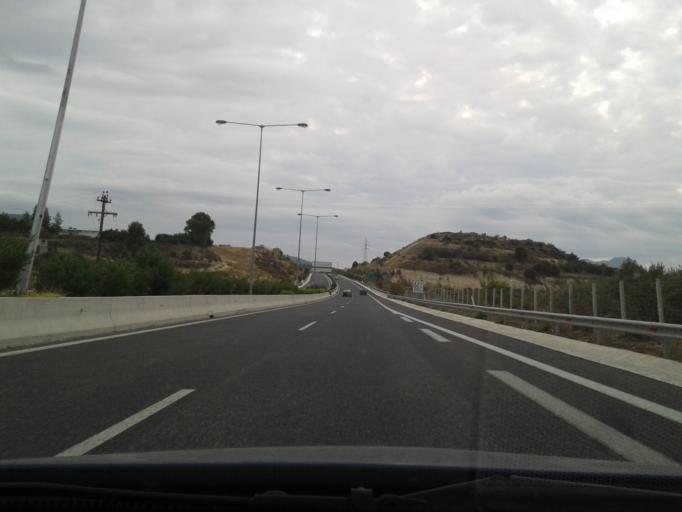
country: GR
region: Peloponnese
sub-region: Nomos Korinthias
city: Arkhaia Korinthos
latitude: 37.9130
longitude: 22.9067
